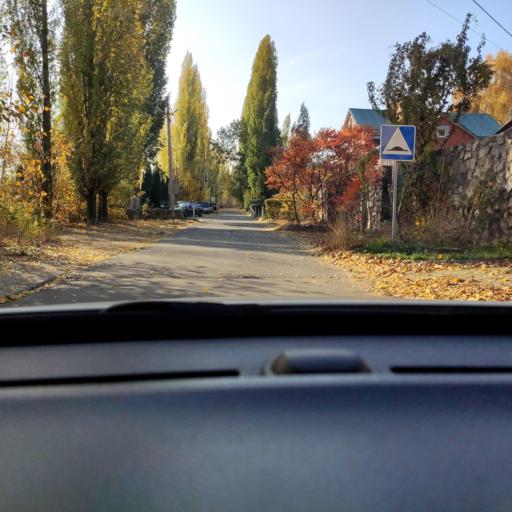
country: RU
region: Voronezj
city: Voronezh
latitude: 51.6990
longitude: 39.2357
